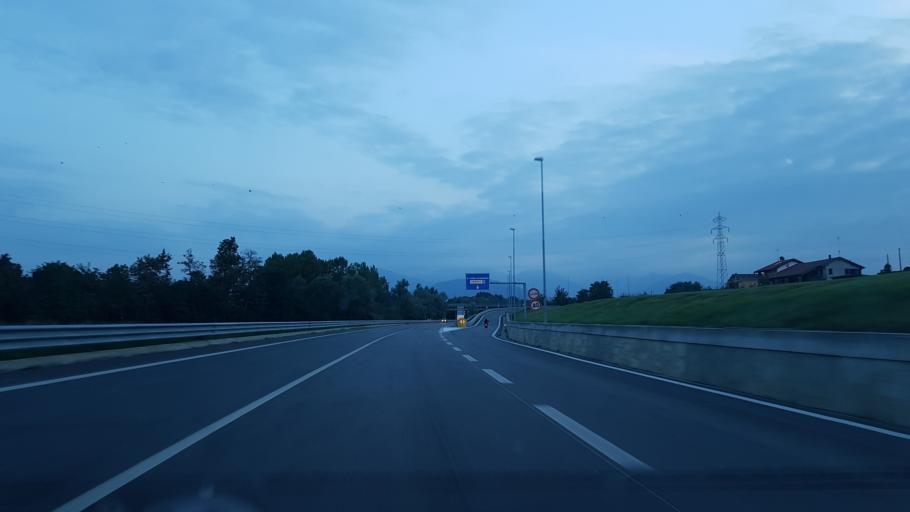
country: IT
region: Piedmont
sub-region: Provincia di Cuneo
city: Mondovi
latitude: 44.3938
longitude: 7.7969
